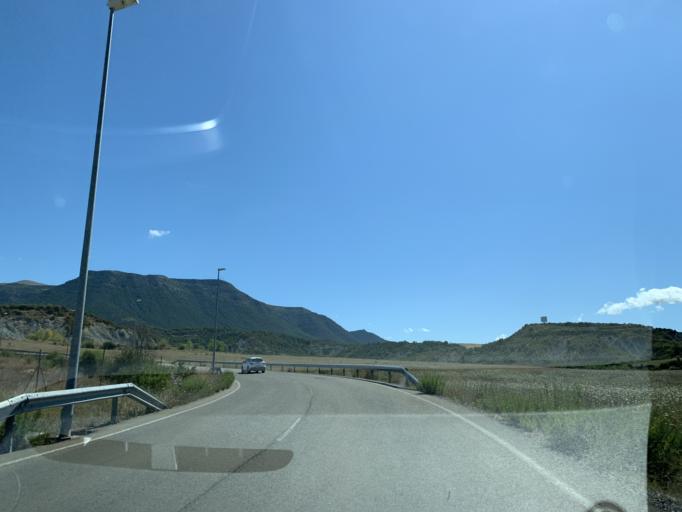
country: ES
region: Aragon
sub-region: Provincia de Huesca
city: Sabinanigo
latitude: 42.5134
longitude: -0.3423
